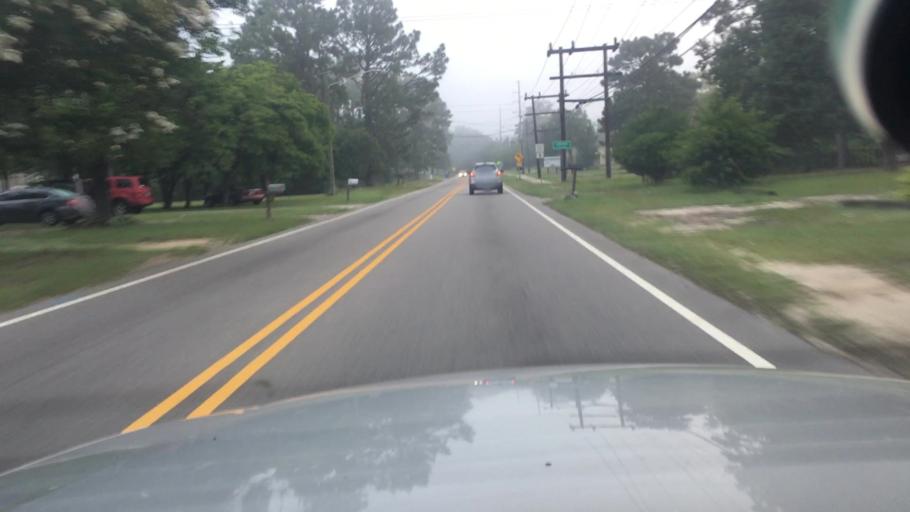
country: US
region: North Carolina
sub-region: Cumberland County
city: Hope Mills
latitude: 35.0191
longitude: -78.9401
